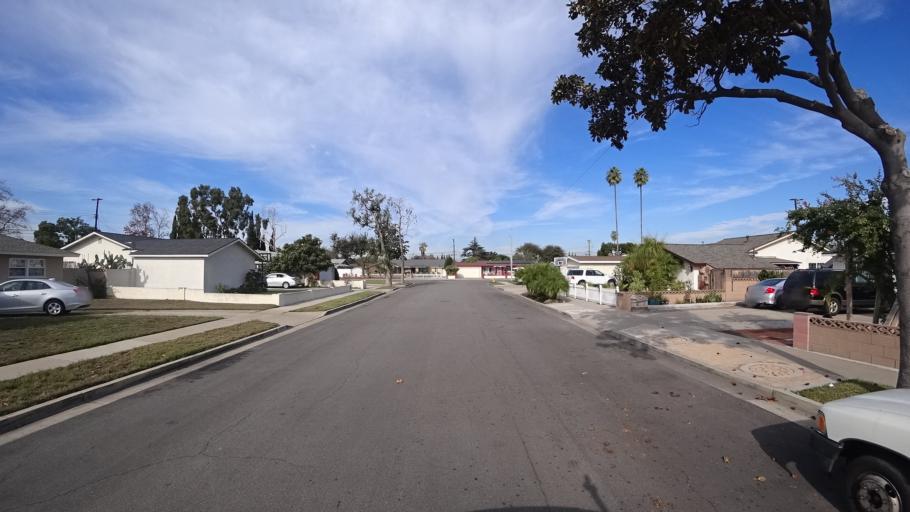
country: US
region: California
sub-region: Orange County
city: Garden Grove
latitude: 33.7826
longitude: -117.9091
